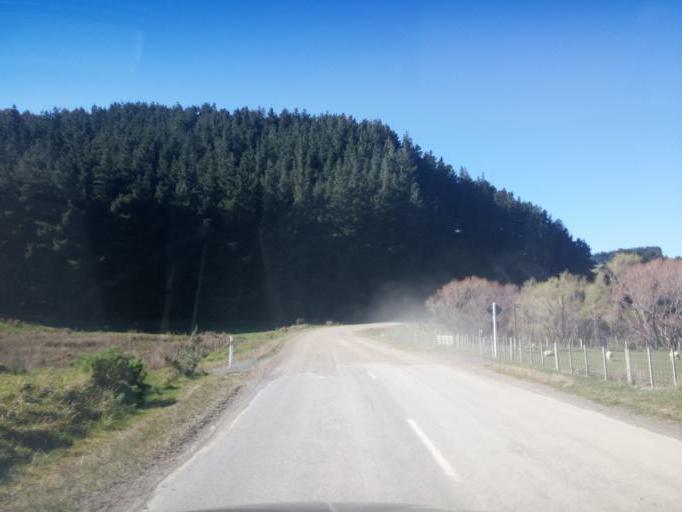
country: NZ
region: Wellington
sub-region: South Wairarapa District
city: Waipawa
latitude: -41.4398
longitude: 175.5188
